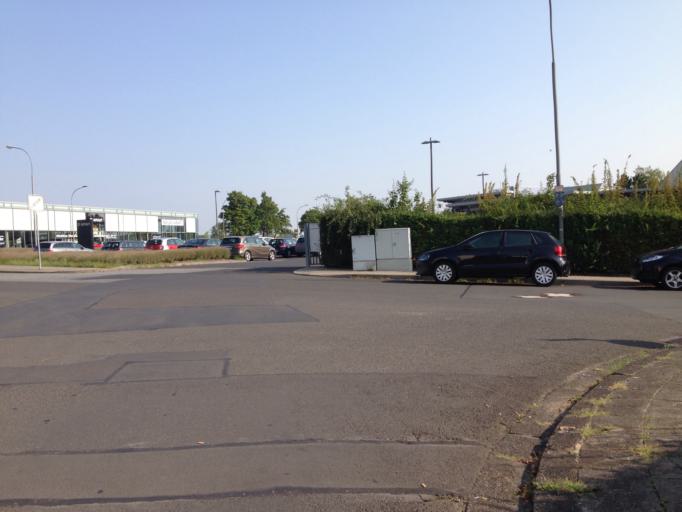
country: DE
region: Hesse
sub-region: Regierungsbezirk Giessen
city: Giessen
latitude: 50.6106
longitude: 8.7020
